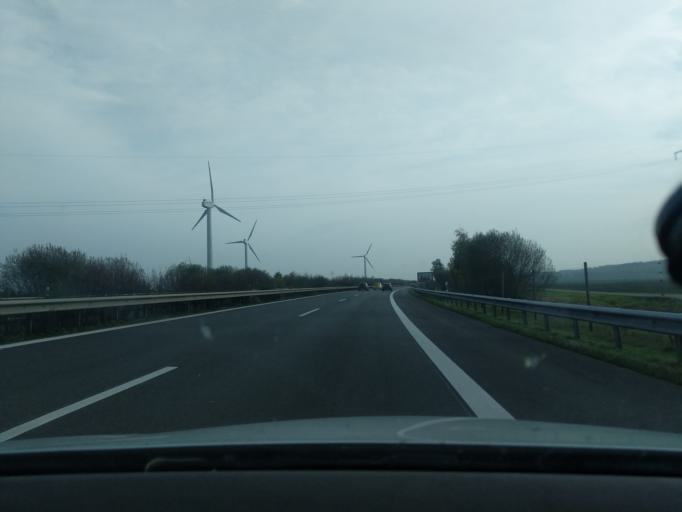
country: DE
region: Lower Saxony
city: Agathenburg
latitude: 53.5649
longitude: 9.5559
